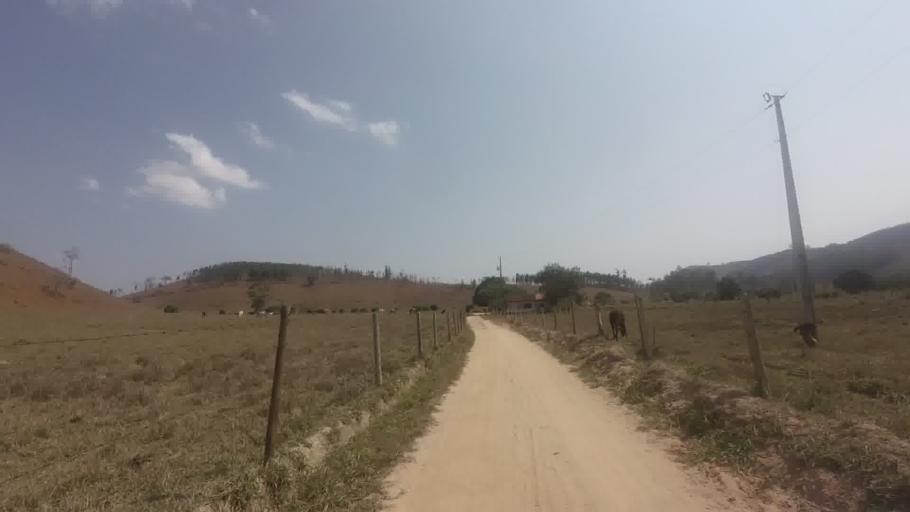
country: BR
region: Espirito Santo
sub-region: Sao Jose Do Calcado
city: Sao Jose do Calcado
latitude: -21.0381
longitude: -41.5265
